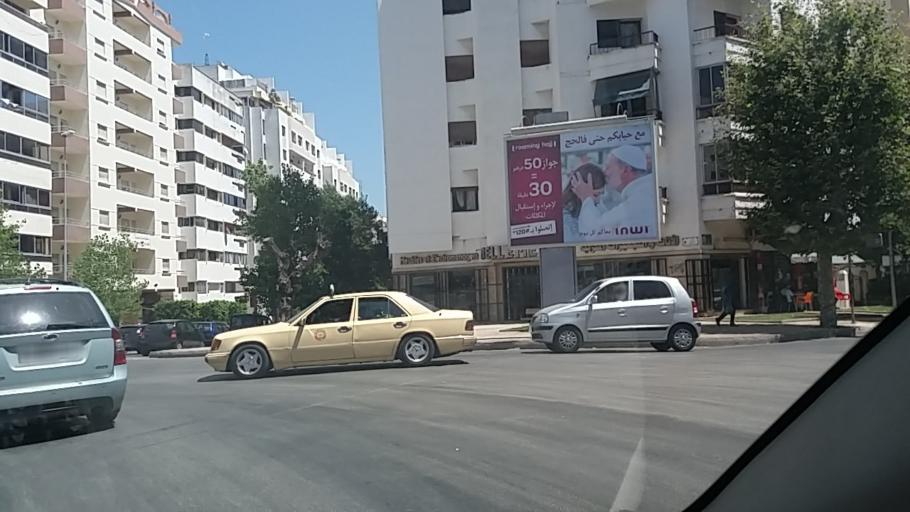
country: MA
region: Tanger-Tetouan
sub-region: Tanger-Assilah
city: Tangier
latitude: 35.7751
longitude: -5.8107
